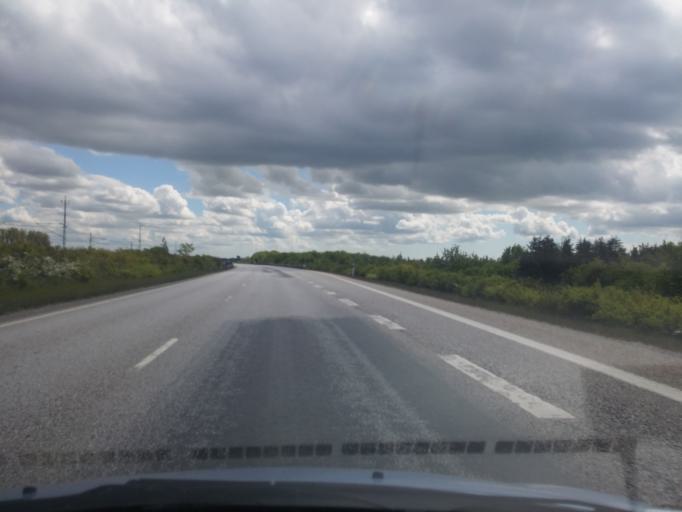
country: SE
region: Skane
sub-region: Malmo
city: Bunkeflostrand
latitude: 55.5524
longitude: 12.9484
